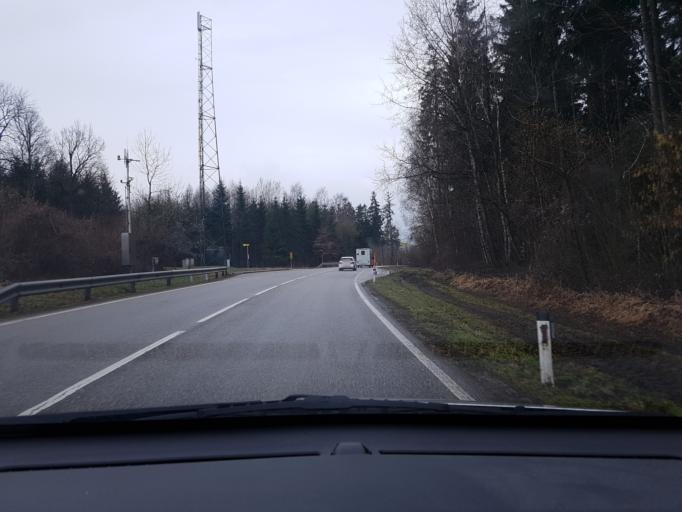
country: AT
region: Upper Austria
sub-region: Steyr Stadt
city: Steyr
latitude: 48.0632
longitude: 14.3887
